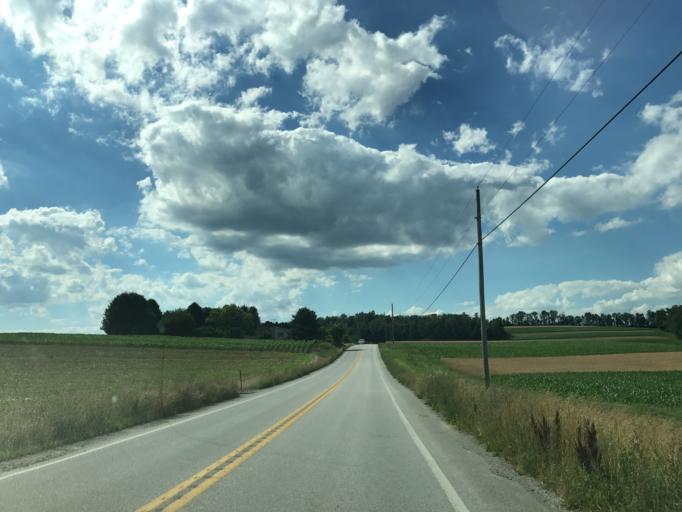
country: US
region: Pennsylvania
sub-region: York County
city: Glen Rock
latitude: 39.7364
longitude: -76.7778
